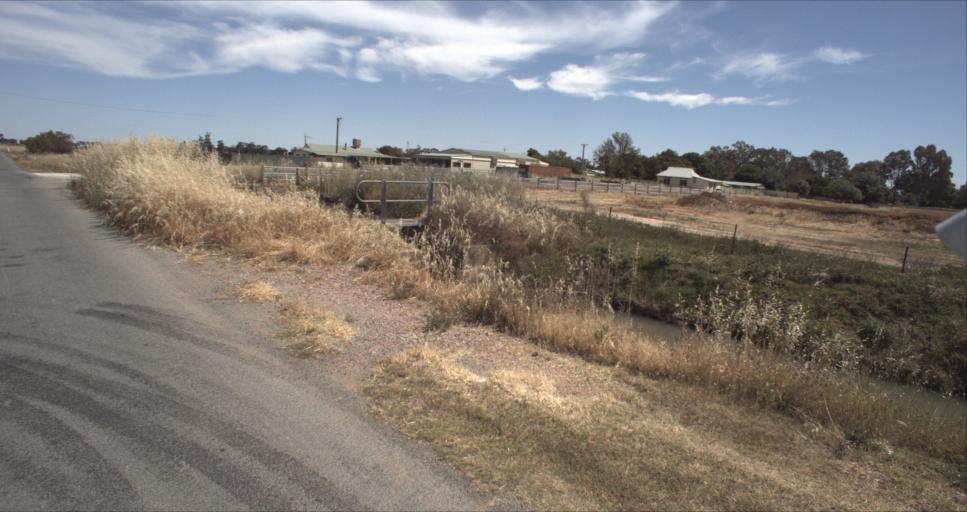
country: AU
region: New South Wales
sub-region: Leeton
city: Leeton
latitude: -34.5843
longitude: 146.4199
